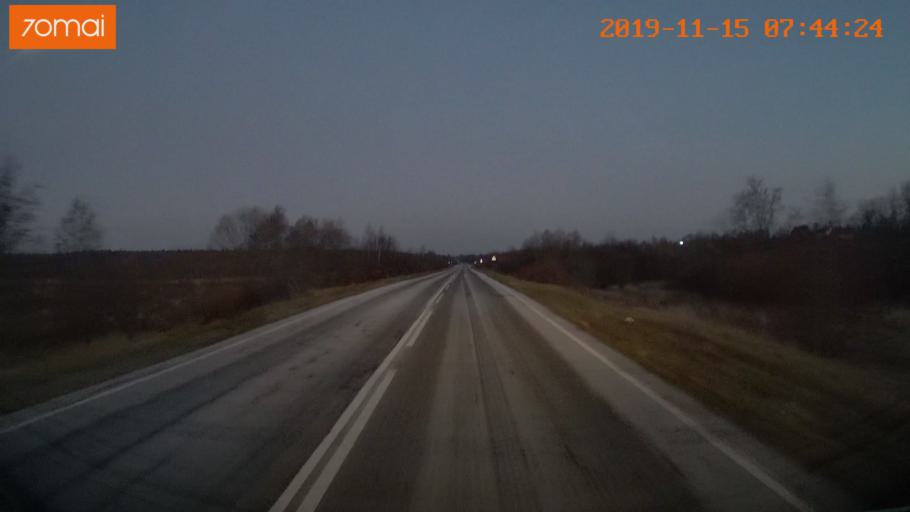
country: RU
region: Vologda
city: Sheksna
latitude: 58.8123
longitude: 38.3146
